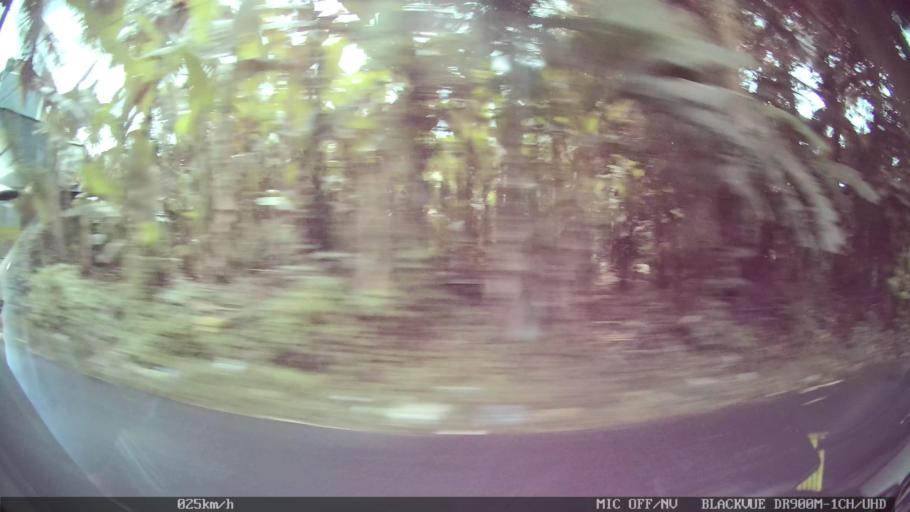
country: ID
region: Bali
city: Banjar Parekan
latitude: -8.5817
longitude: 115.2121
